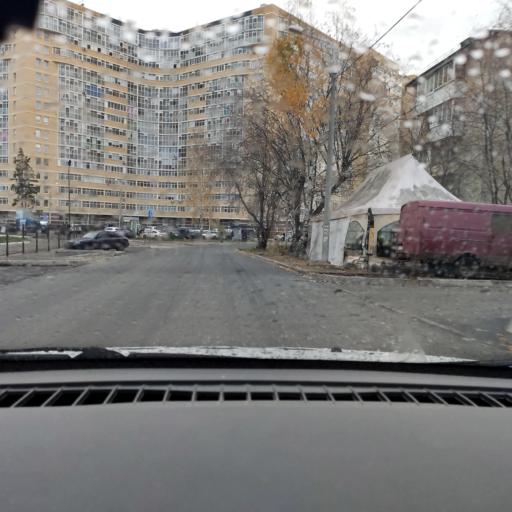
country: RU
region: Perm
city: Kondratovo
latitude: 58.0482
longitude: 56.0871
